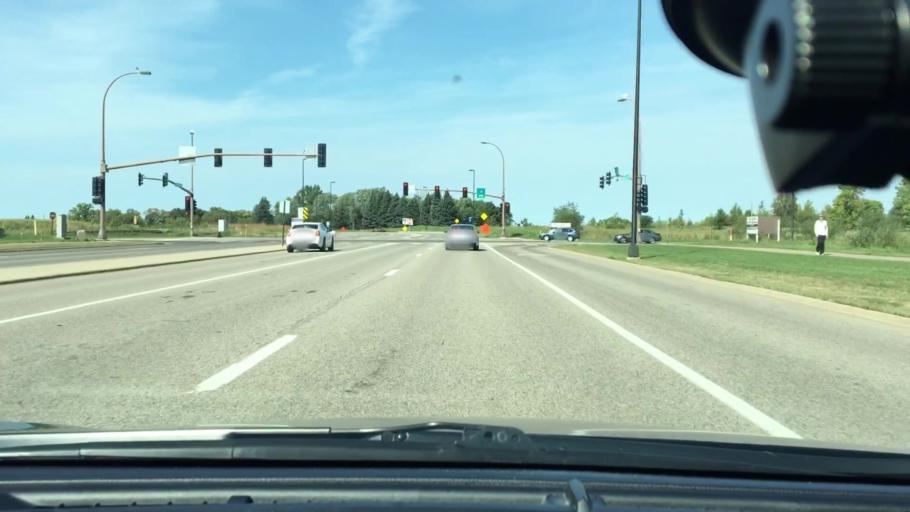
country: US
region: Minnesota
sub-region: Hennepin County
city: Corcoran
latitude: 45.0854
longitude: -93.5163
